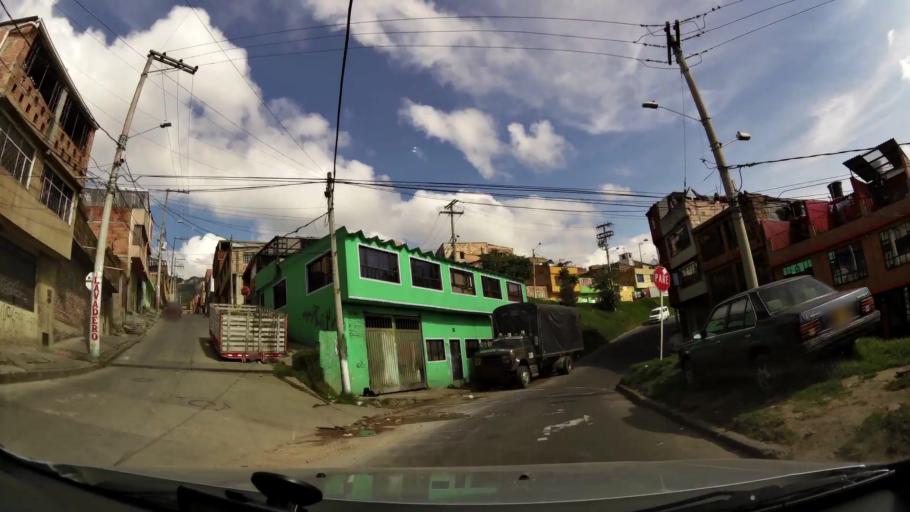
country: CO
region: Bogota D.C.
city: Bogota
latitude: 4.5455
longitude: -74.0895
